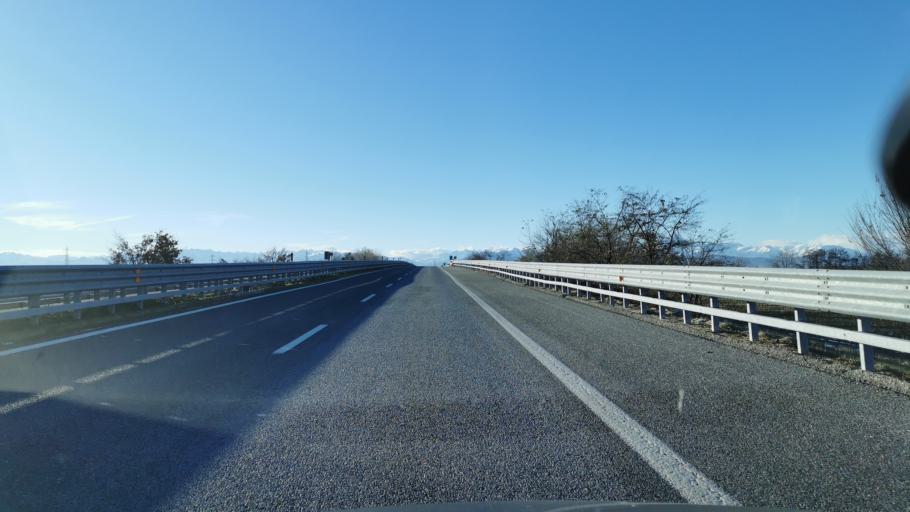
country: IT
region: Piedmont
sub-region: Provincia di Cuneo
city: Trinita
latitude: 44.4696
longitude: 7.7527
